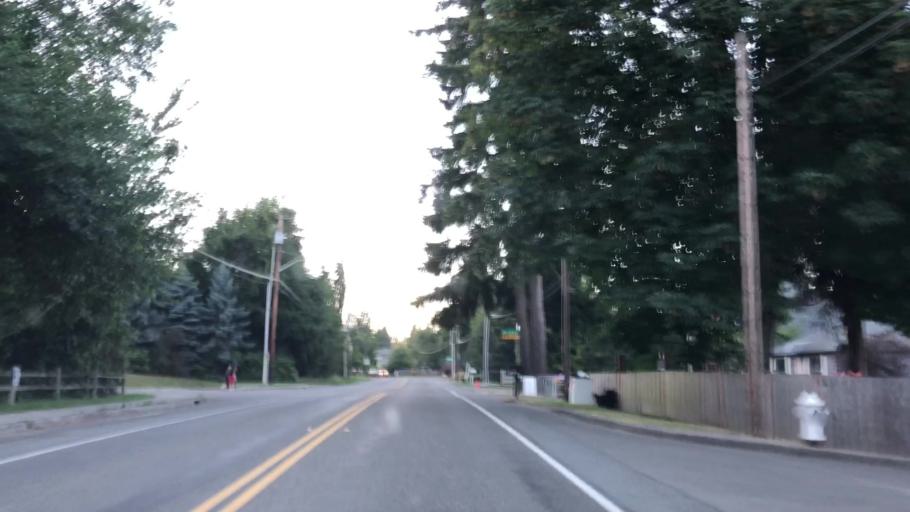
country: US
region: Washington
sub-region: Snohomish County
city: Brier
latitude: 47.7723
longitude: -122.2697
